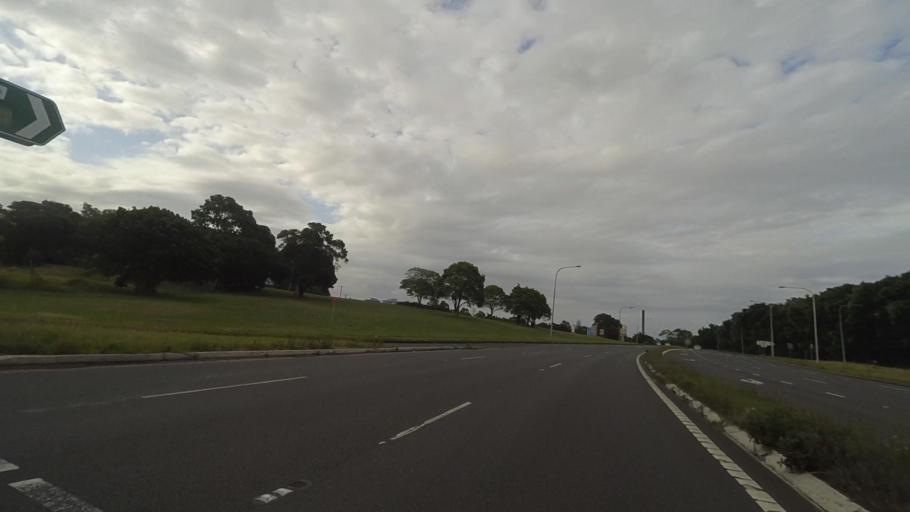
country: AU
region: New South Wales
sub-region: Wollongong
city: Cringila
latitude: -34.4784
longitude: 150.8868
